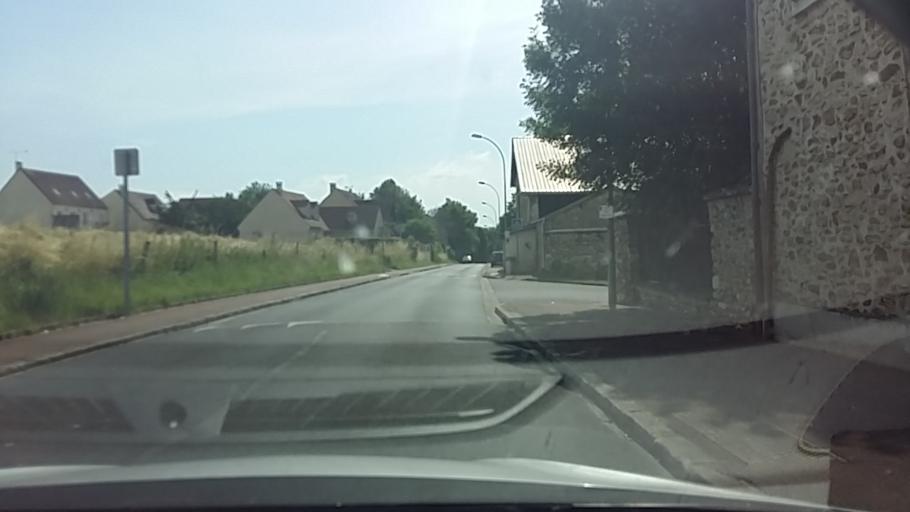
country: FR
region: Ile-de-France
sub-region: Departement du Val-de-Marne
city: Noiseau
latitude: 48.7778
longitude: 2.5444
